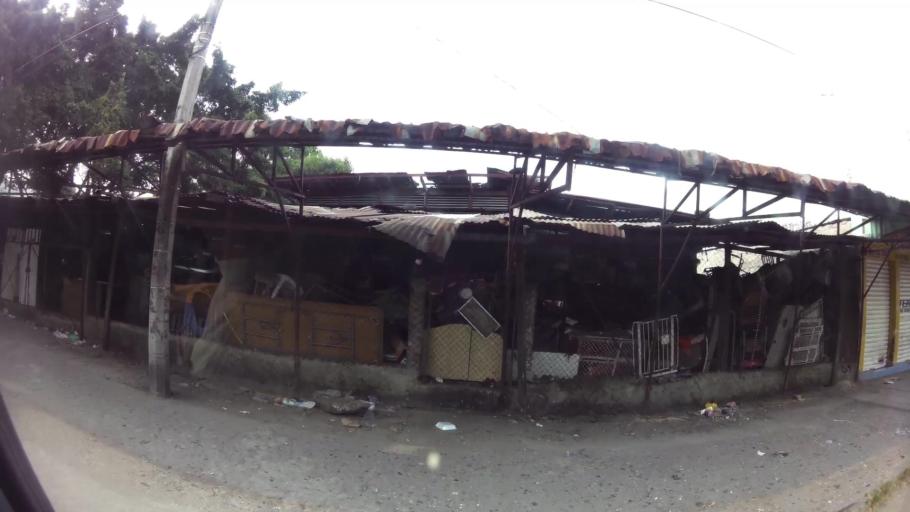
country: HN
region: Cortes
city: San Pedro Sula
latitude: 15.4994
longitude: -88.0167
